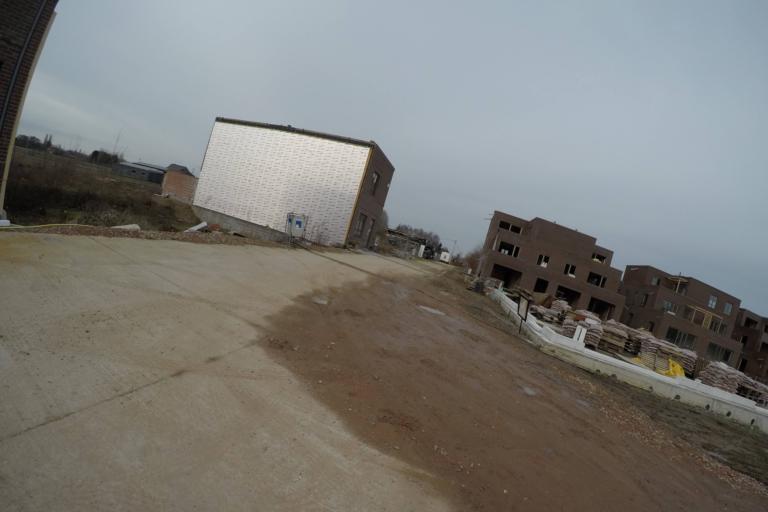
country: BE
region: Flanders
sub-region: Provincie Antwerpen
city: Wommelgem
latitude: 51.1990
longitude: 4.5150
